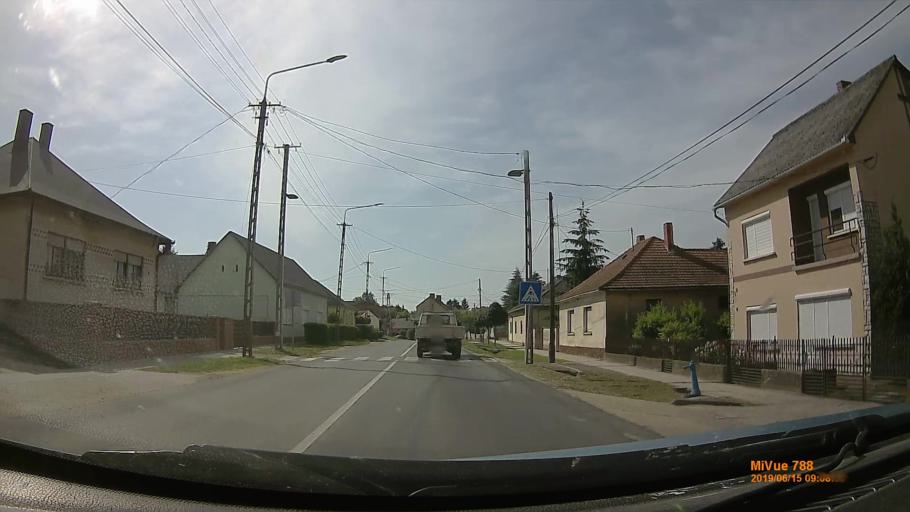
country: HU
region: Tolna
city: Iregszemcse
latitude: 46.6961
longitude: 18.1825
